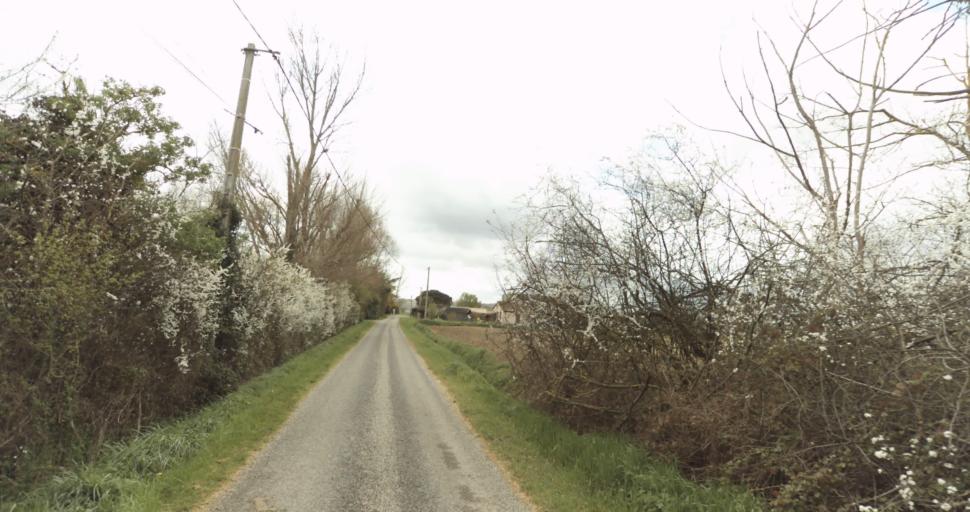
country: FR
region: Midi-Pyrenees
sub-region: Departement de la Haute-Garonne
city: Auterive
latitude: 43.3272
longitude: 1.4708
